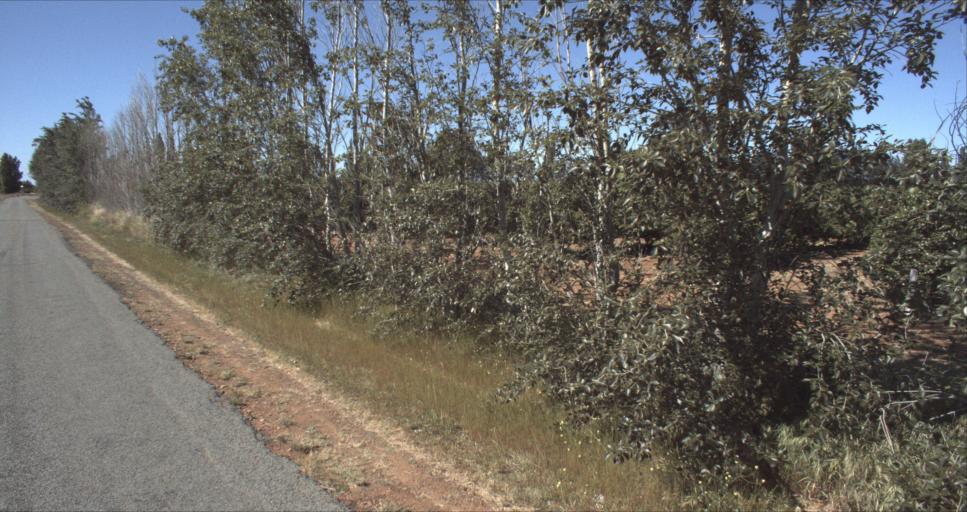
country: AU
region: New South Wales
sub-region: Leeton
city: Leeton
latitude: -34.5419
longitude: 146.3423
